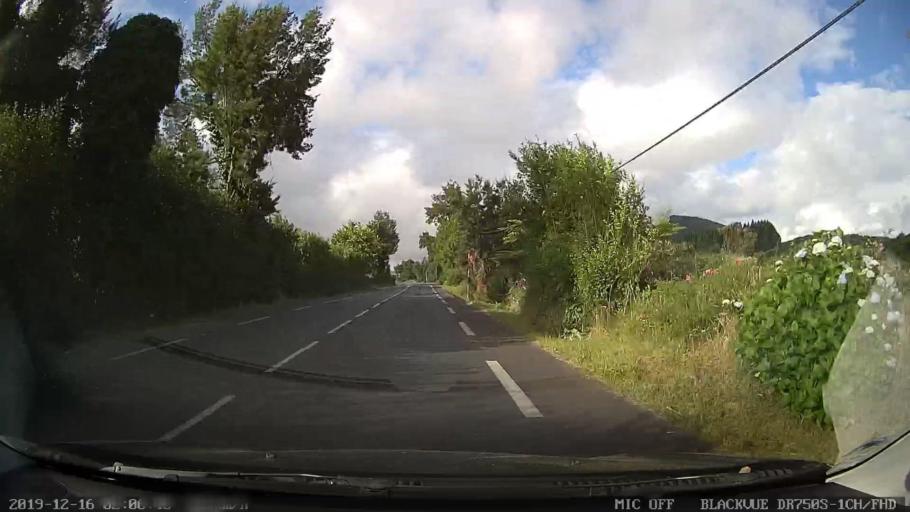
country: RE
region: Reunion
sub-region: Reunion
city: Le Tampon
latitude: -21.1880
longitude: 55.5799
